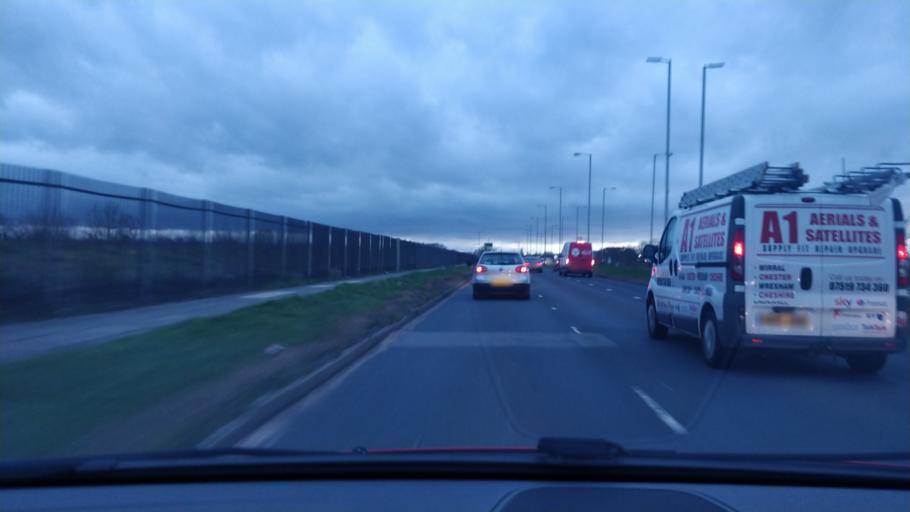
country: GB
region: England
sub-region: Knowsley
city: Kirkby
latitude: 53.4606
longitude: -2.9026
